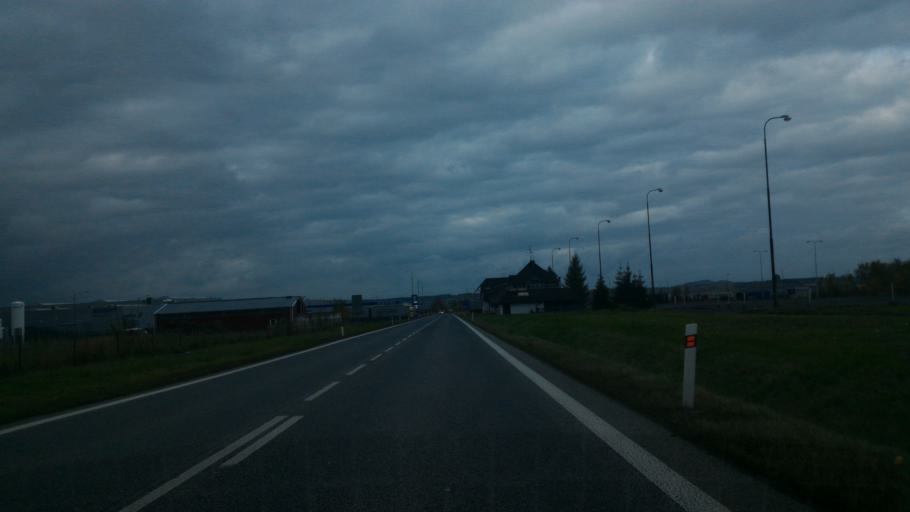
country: CZ
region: Ustecky
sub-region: Okres Decin
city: Rumburk
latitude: 50.9288
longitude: 14.5590
